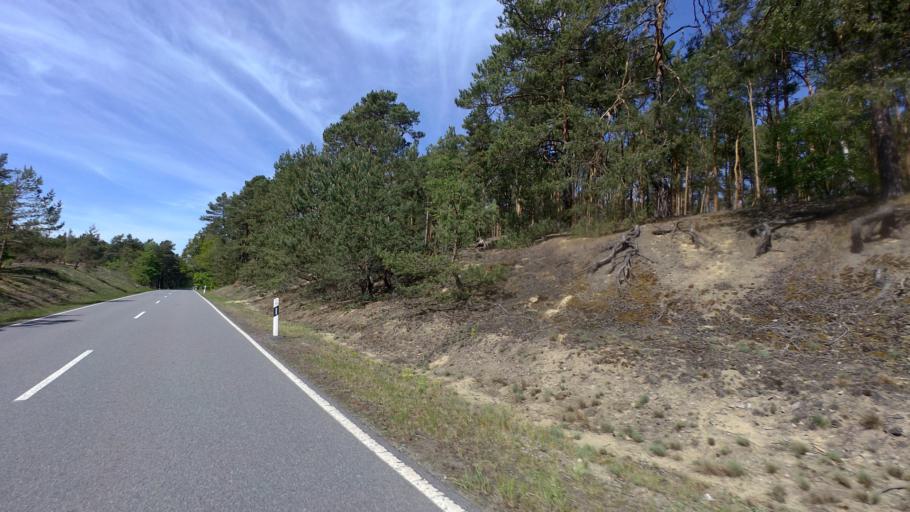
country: DE
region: Brandenburg
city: Sperenberg
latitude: 52.0896
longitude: 13.3905
